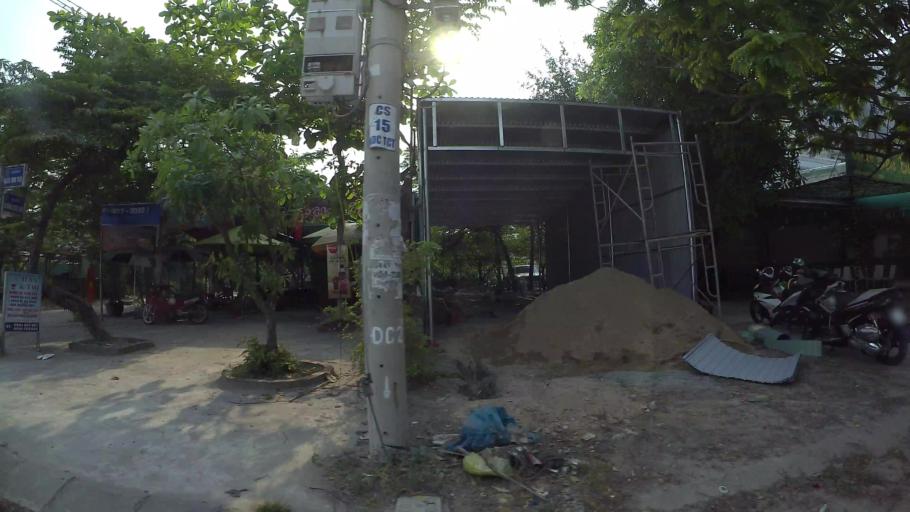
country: VN
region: Da Nang
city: Lien Chieu
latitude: 16.0502
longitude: 108.1602
